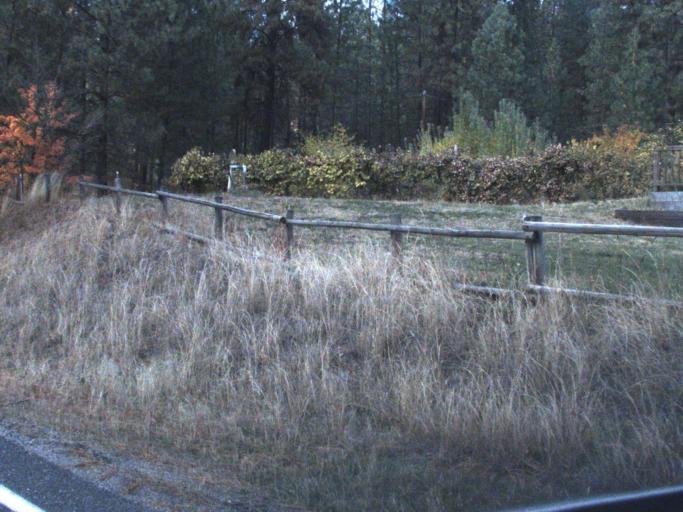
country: US
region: Washington
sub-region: Stevens County
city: Kettle Falls
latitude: 48.7227
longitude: -118.0329
